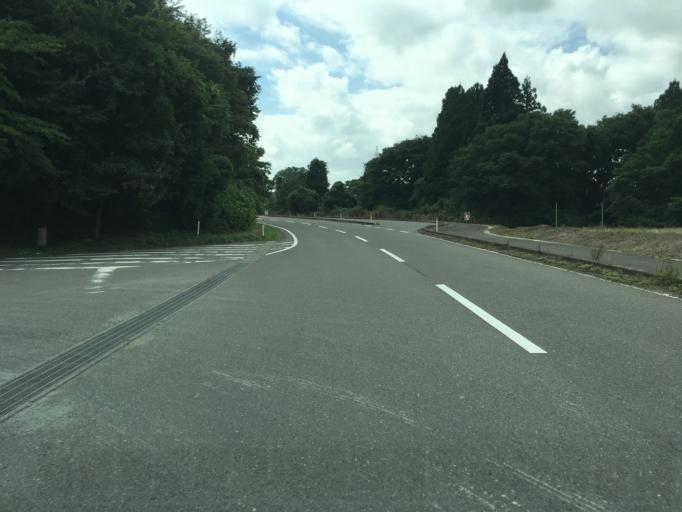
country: JP
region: Fukushima
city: Motomiya
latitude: 37.4777
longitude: 140.3371
